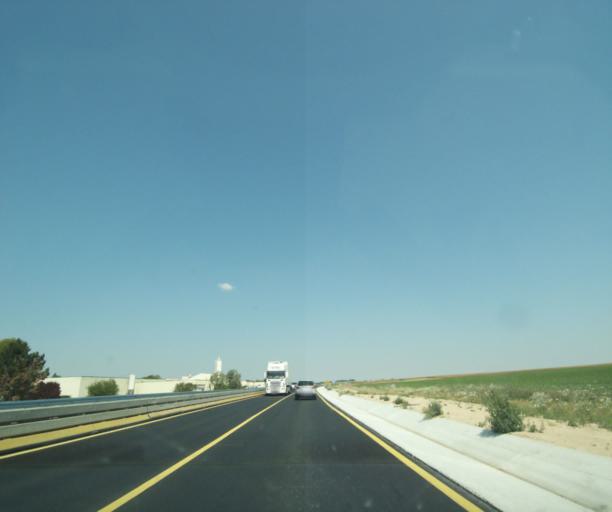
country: FR
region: Champagne-Ardenne
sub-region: Departement de la Marne
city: Sarry
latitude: 48.8828
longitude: 4.4628
